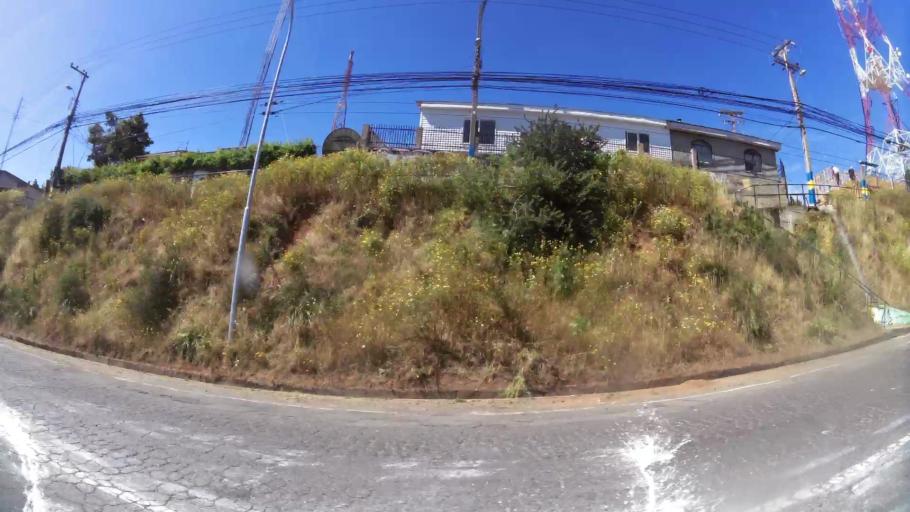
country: CL
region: Valparaiso
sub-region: Provincia de Valparaiso
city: Vina del Mar
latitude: -33.0443
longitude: -71.5669
